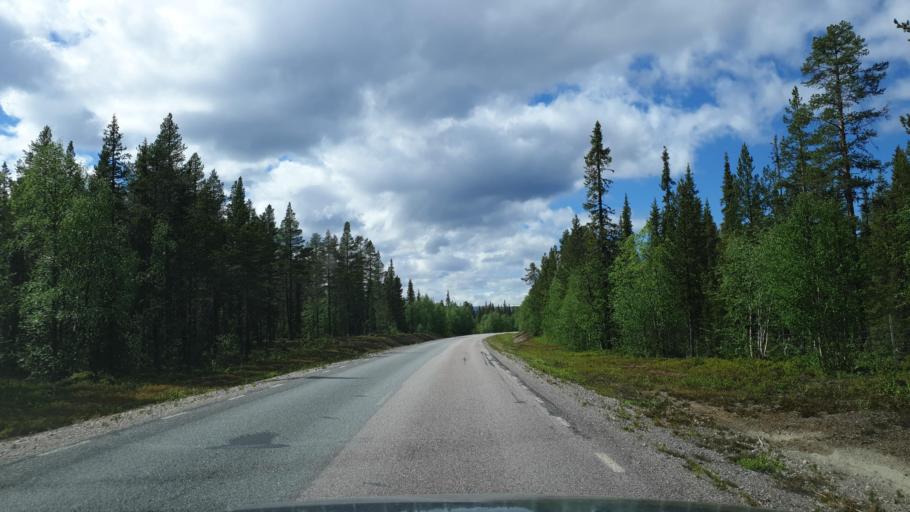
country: SE
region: Norrbotten
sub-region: Jokkmokks Kommun
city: Jokkmokk
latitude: 67.2162
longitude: 19.2895
